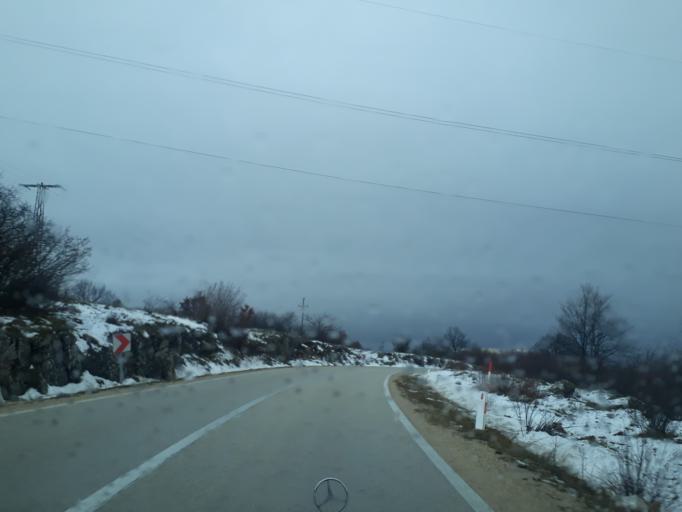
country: BA
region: Federation of Bosnia and Herzegovina
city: Tomislavgrad
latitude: 43.7873
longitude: 17.2228
